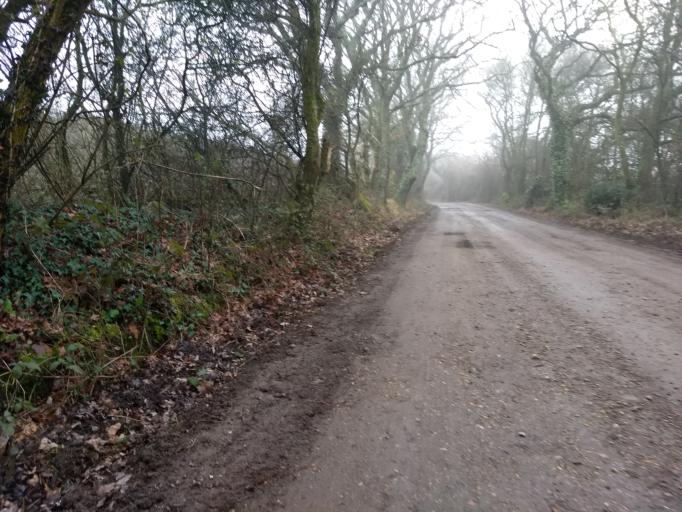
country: GB
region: England
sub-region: Isle of Wight
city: Newport
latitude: 50.7024
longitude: -1.2634
